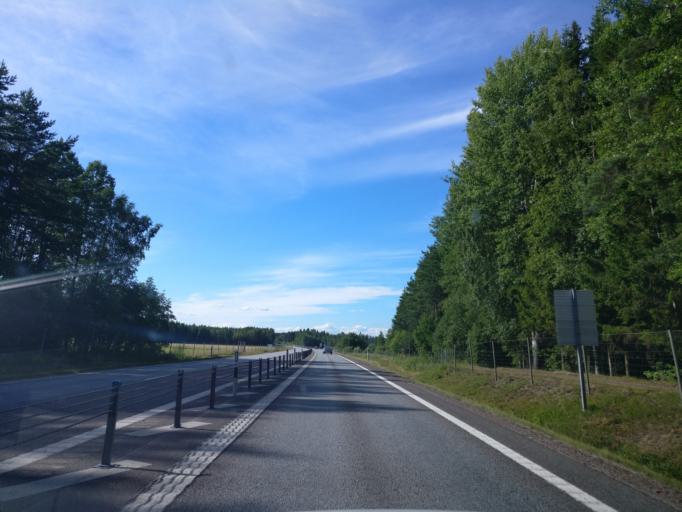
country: SE
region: Vaermland
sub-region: Kils Kommun
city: Kil
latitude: 59.4790
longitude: 13.3585
